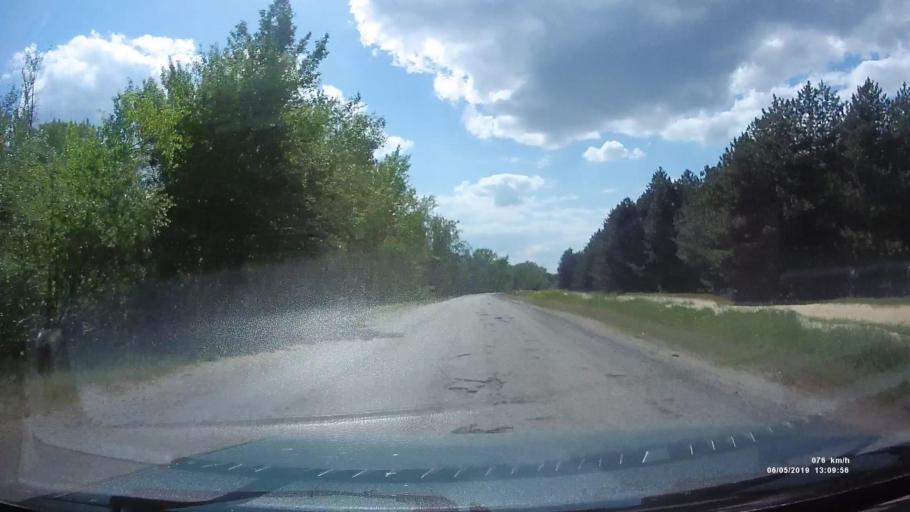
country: RU
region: Rostov
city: Ust'-Donetskiy
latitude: 47.7645
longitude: 40.9778
